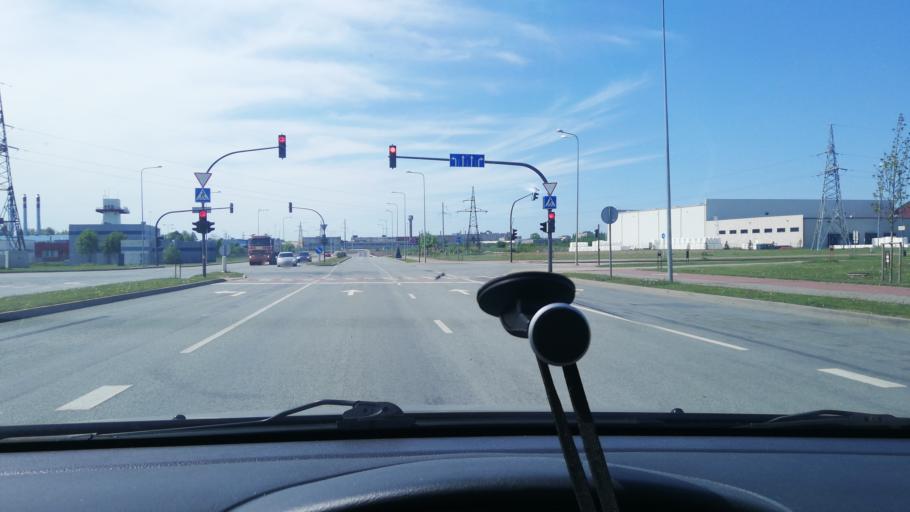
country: LT
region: Klaipedos apskritis
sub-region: Klaipeda
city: Klaipeda
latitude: 55.6867
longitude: 21.2060
